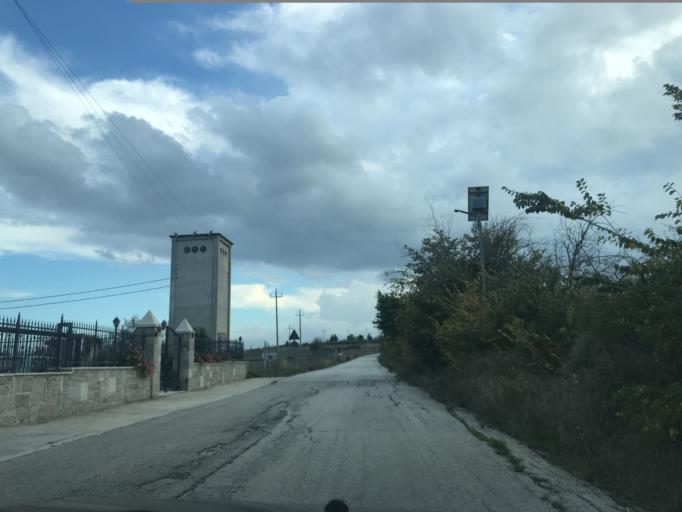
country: IT
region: Molise
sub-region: Provincia di Isernia
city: Bagnoli del Trigno
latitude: 41.6946
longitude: 14.4618
